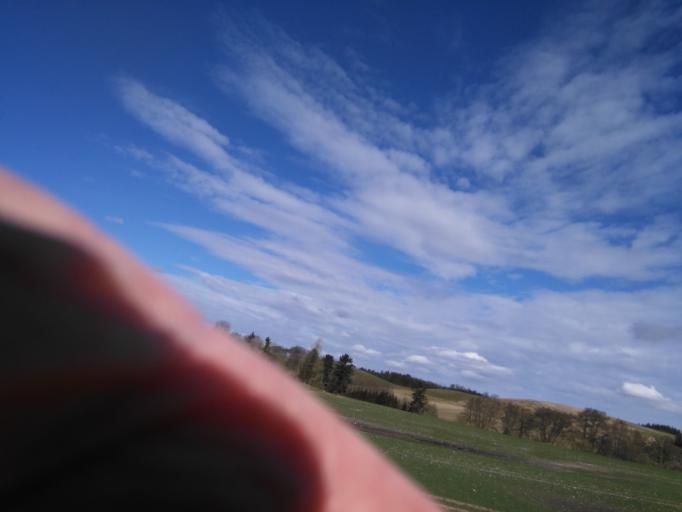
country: DK
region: Central Jutland
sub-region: Odder Kommune
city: Odder
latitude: 55.8908
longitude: 10.0284
